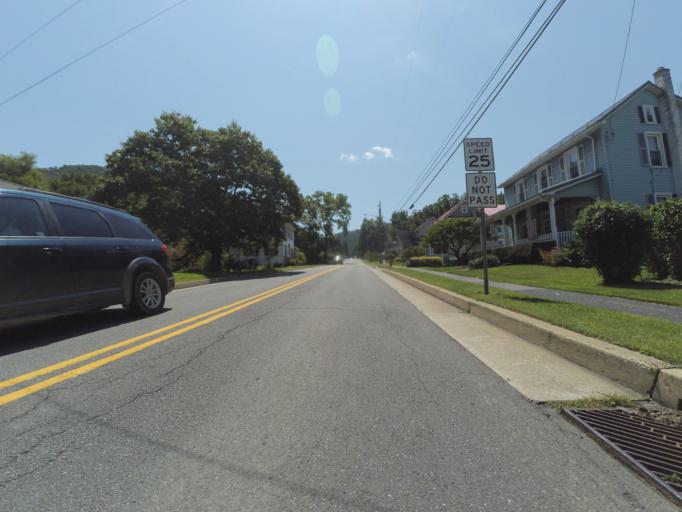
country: US
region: Pennsylvania
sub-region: Centre County
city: Pleasant Gap
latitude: 40.8644
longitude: -77.7340
